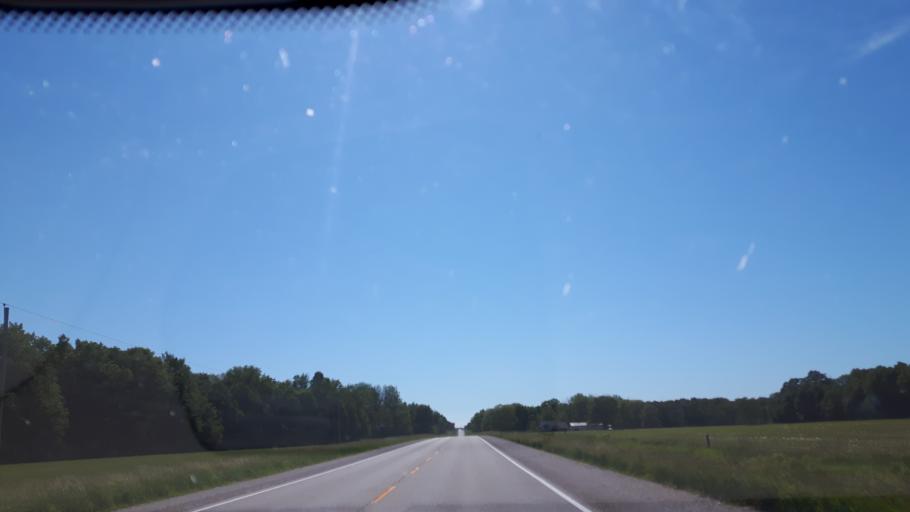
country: CA
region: Ontario
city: Bluewater
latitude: 43.4298
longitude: -81.5433
